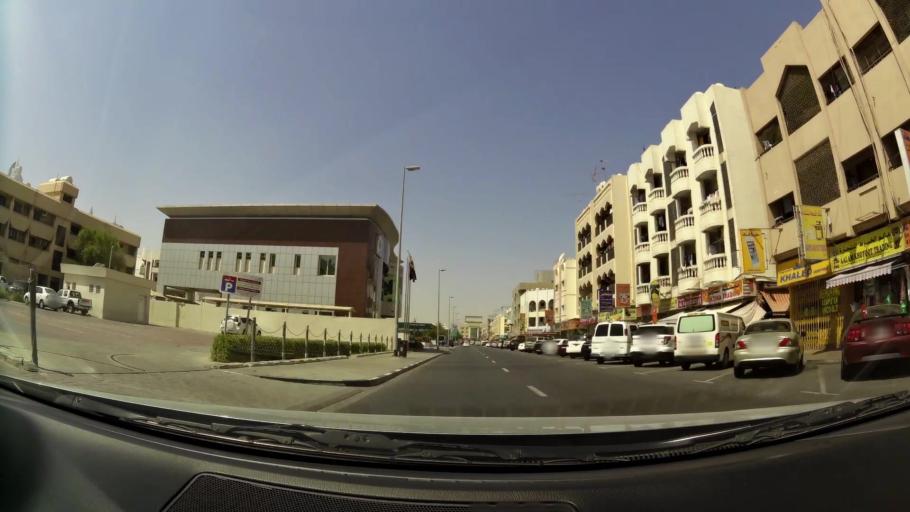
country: AE
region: Ash Shariqah
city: Sharjah
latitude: 25.2302
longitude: 55.2753
